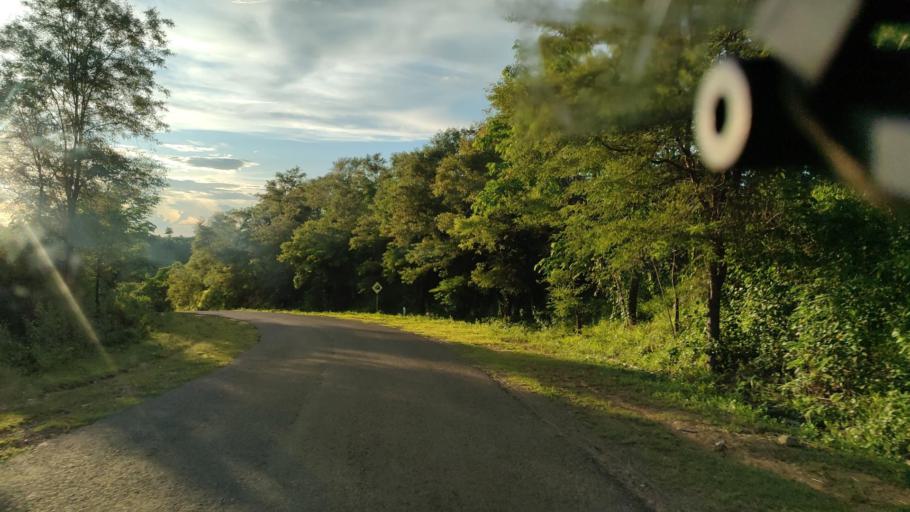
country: MM
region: Magway
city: Taungdwingyi
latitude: 20.1085
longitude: 95.7433
